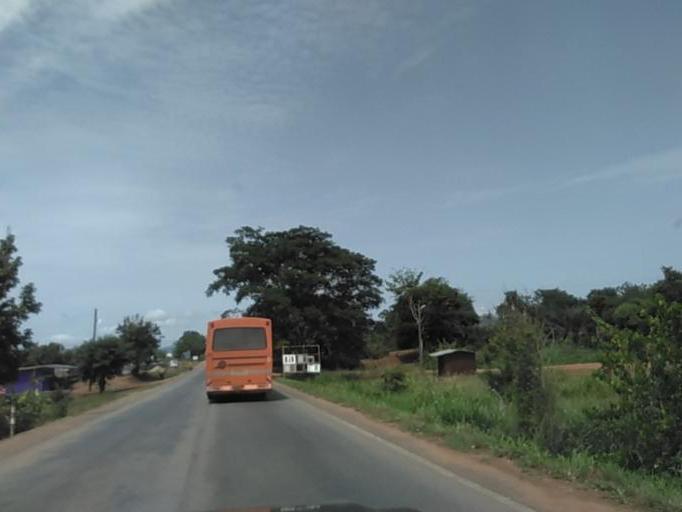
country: GH
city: Akropong
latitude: 6.1965
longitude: 0.0770
